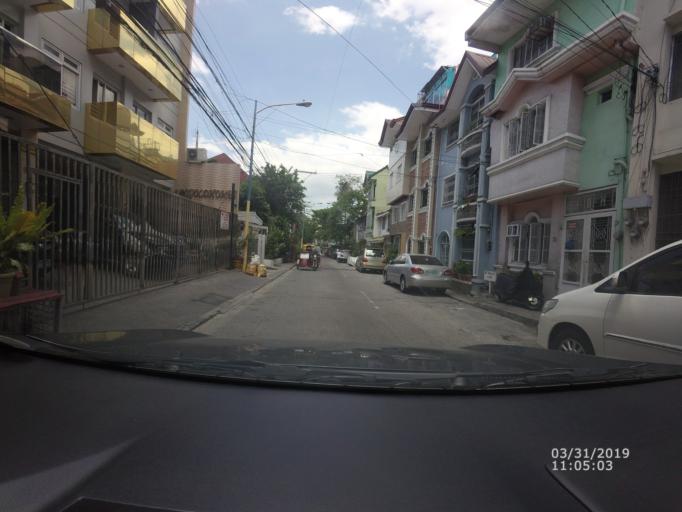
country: PH
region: Metro Manila
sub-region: Mandaluyong
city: Mandaluyong City
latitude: 14.5786
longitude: 121.0391
